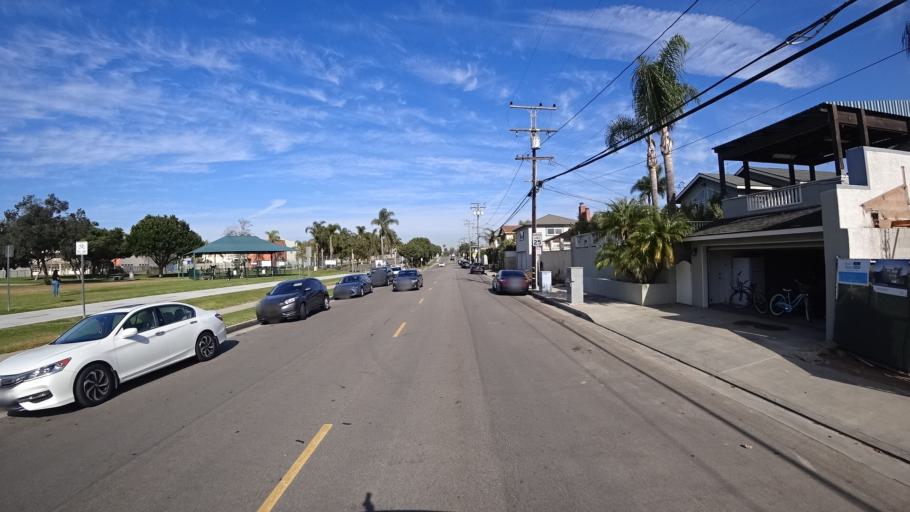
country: US
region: California
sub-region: Los Angeles County
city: Manhattan Beach
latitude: 33.8880
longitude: -118.3831
